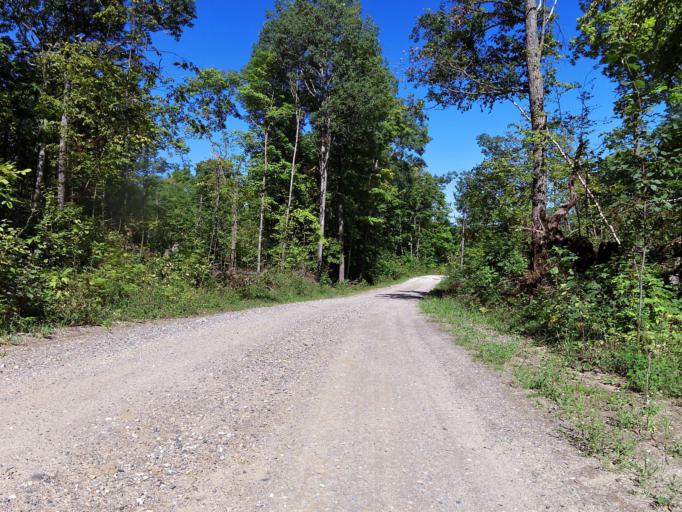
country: CA
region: Ontario
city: Renfrew
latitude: 45.1342
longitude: -76.7076
